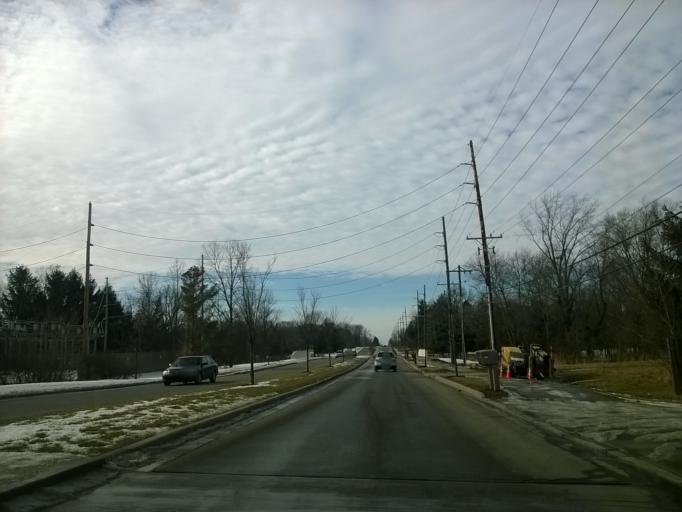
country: US
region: Indiana
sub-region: Hamilton County
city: Carmel
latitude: 39.9778
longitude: -86.1686
